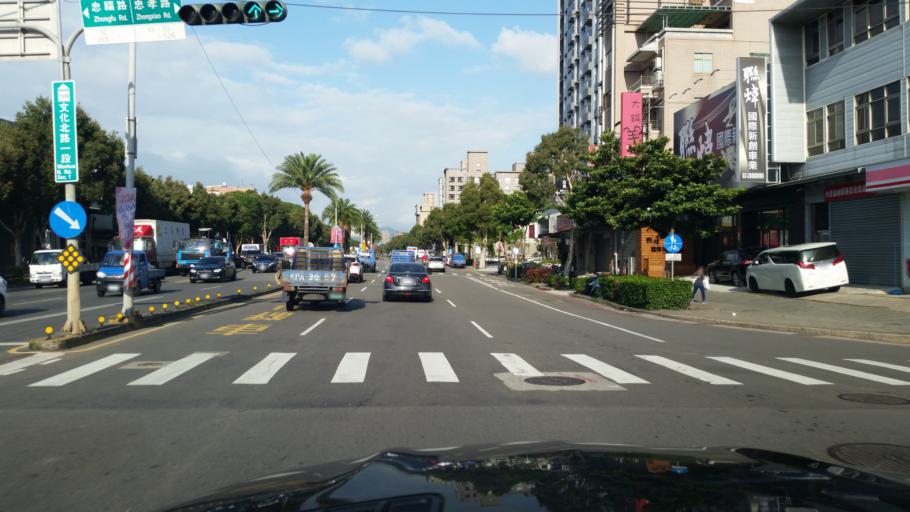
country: TW
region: Taiwan
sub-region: Taoyuan
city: Taoyuan
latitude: 25.0759
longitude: 121.3641
